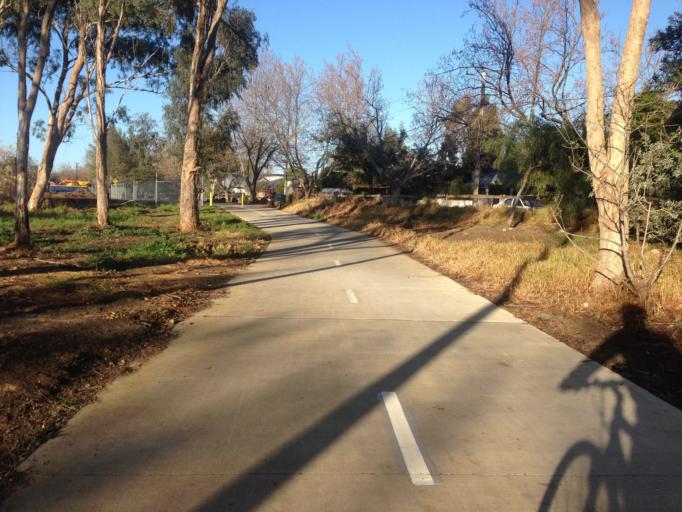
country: AU
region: Victoria
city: Alphington
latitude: -37.7755
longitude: 145.0321
